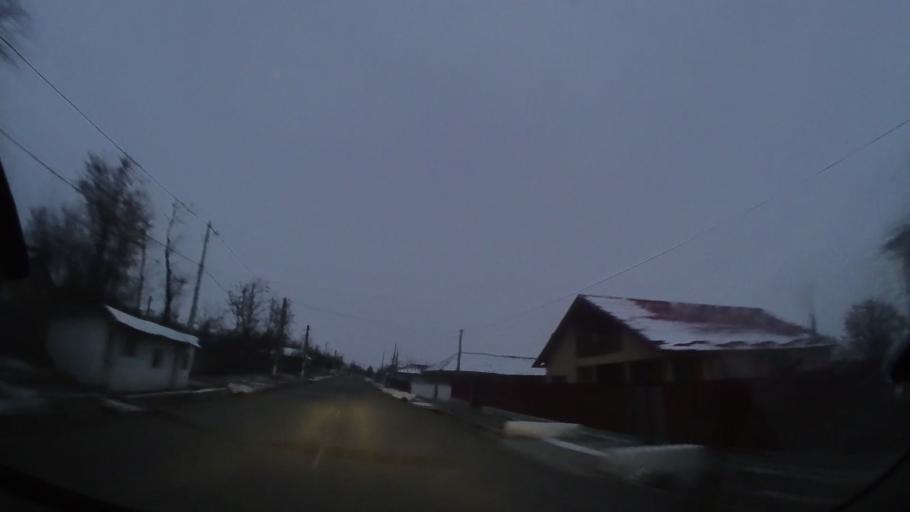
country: RO
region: Vaslui
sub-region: Comuna Dimitrie Cantemir
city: Dimitrie Cantemir
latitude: 46.4591
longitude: 28.0268
